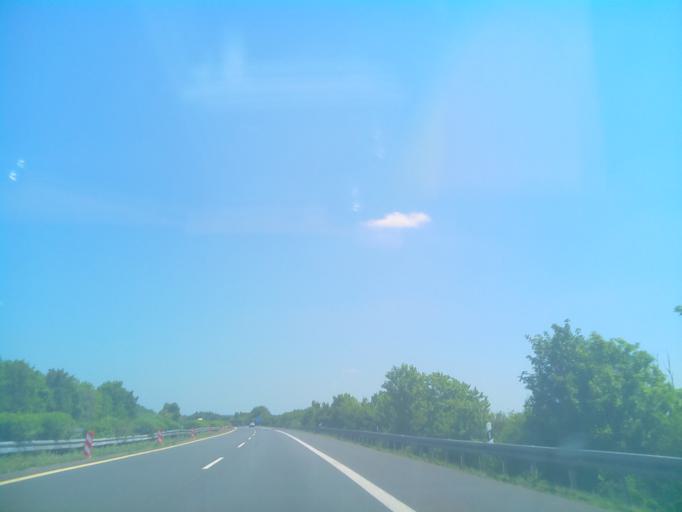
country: DE
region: Baden-Wuerttemberg
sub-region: Regierungsbezirk Stuttgart
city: Grossrinderfeld
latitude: 49.6631
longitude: 9.7615
